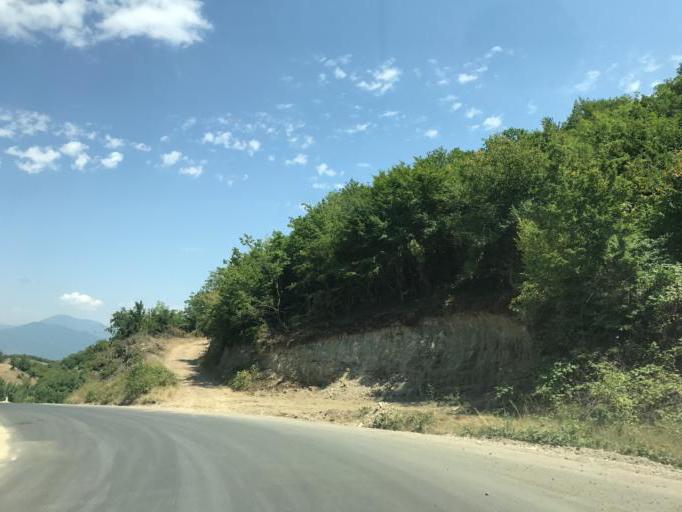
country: AZ
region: Tartar Rayon
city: Martakert
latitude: 40.1287
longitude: 46.6253
